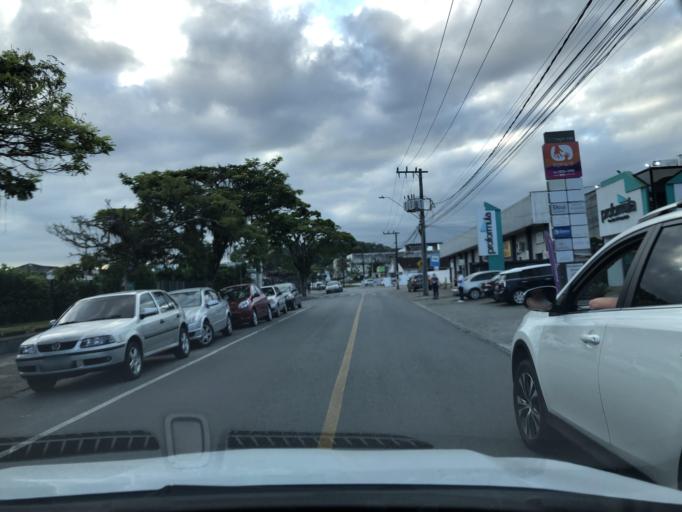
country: BR
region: Santa Catarina
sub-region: Joinville
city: Joinville
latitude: -26.2887
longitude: -48.8457
